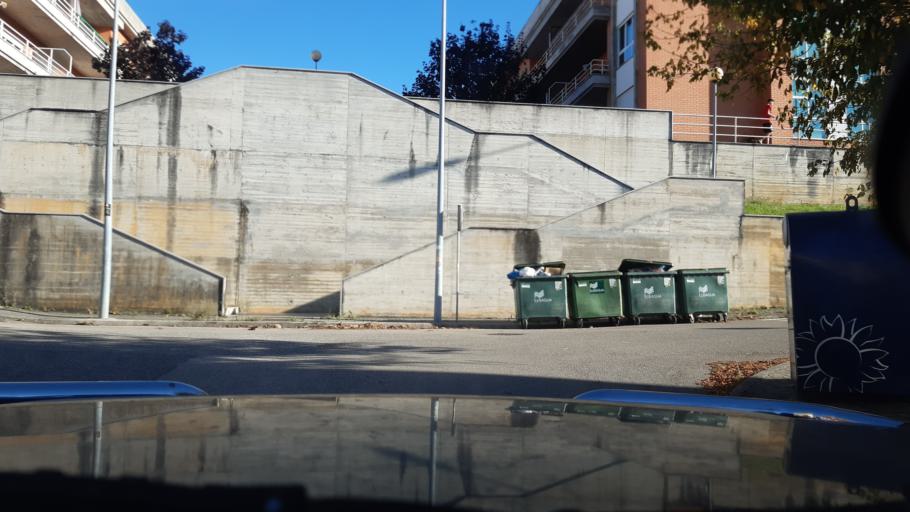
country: PT
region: Aveiro
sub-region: Agueda
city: Agueda
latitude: 40.5539
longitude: -8.4393
